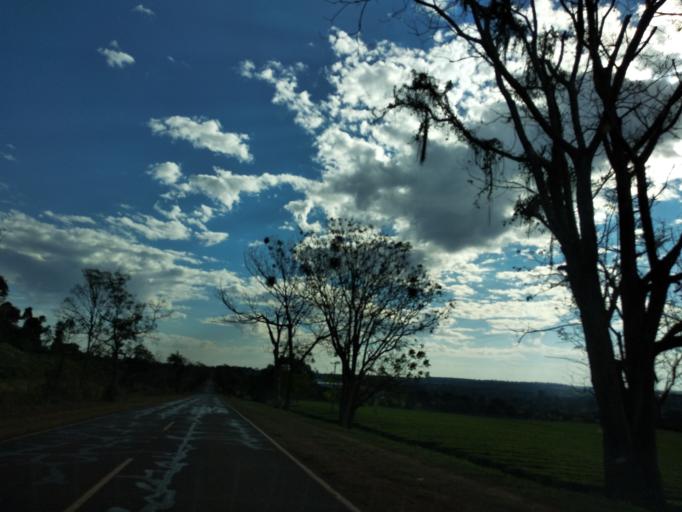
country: AR
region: Misiones
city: Jardin America
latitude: -27.0364
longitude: -55.2109
